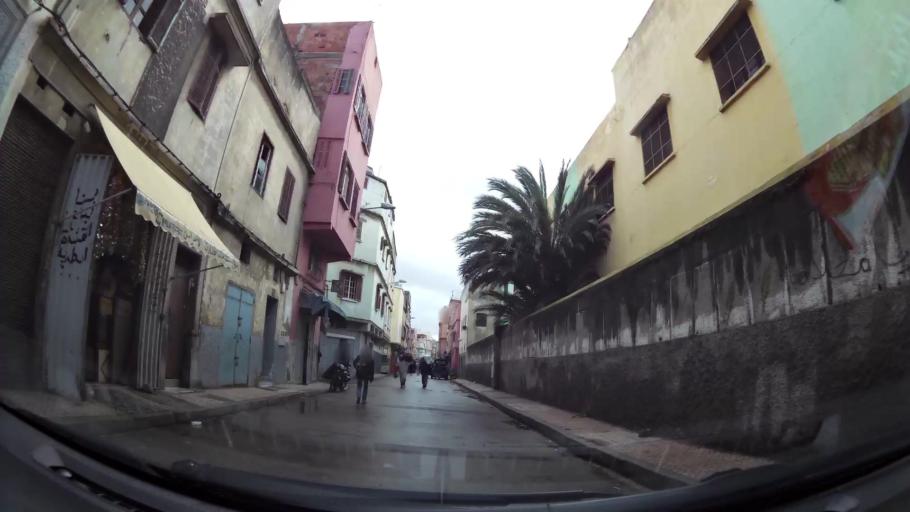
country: MA
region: Grand Casablanca
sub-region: Casablanca
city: Casablanca
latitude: 33.5718
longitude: -7.6000
